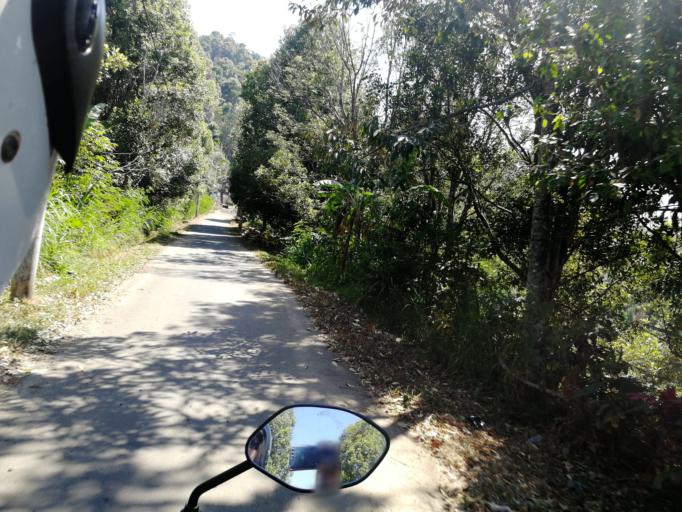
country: ID
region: Bali
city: Banjar Kedisan
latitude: -8.1675
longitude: 115.3023
